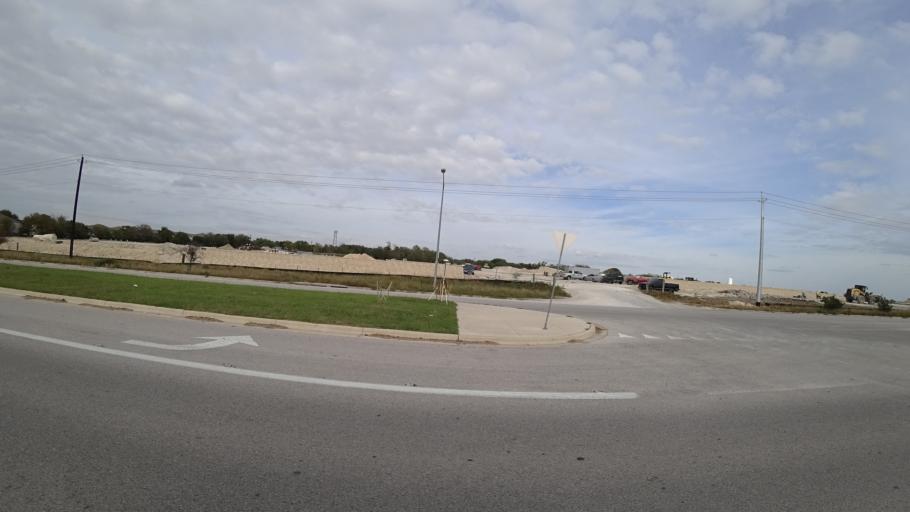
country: US
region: Texas
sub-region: Travis County
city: Windemere
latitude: 30.4363
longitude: -97.6561
